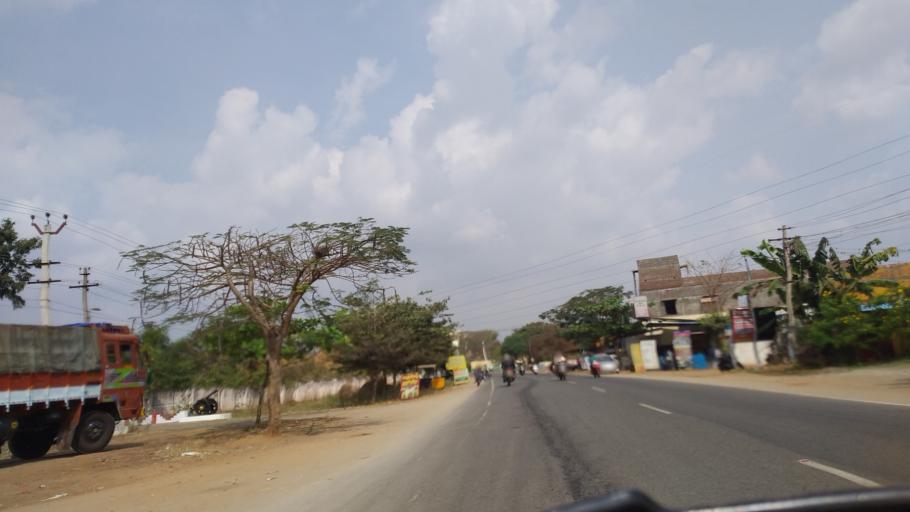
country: IN
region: Tamil Nadu
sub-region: Coimbatore
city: Madukkarai
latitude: 10.9404
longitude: 76.9432
